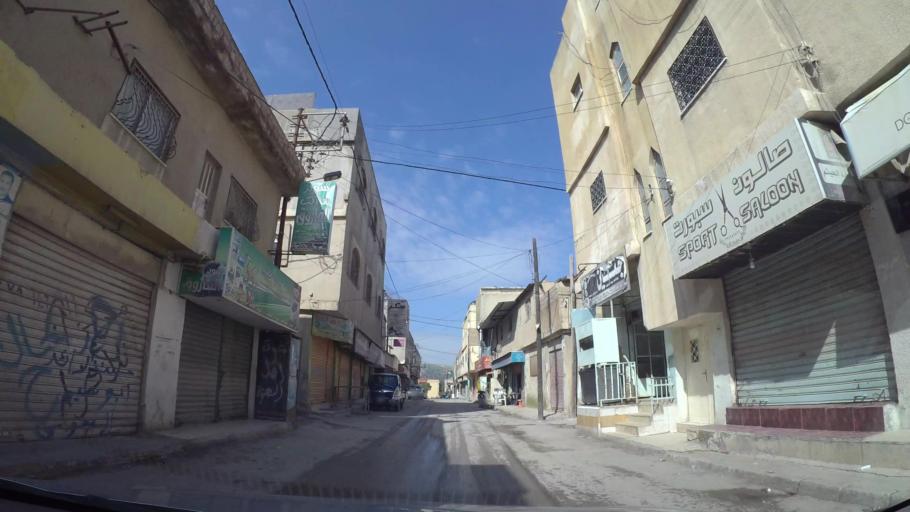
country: JO
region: Amman
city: Al Jubayhah
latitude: 32.0733
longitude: 35.8397
